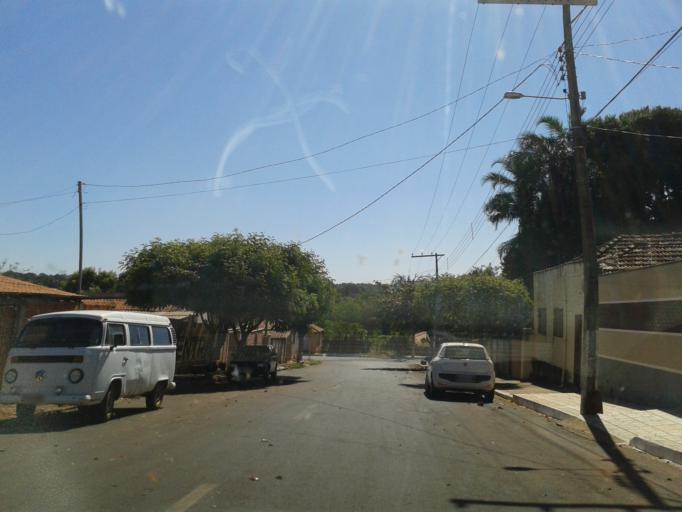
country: BR
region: Minas Gerais
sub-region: Santa Vitoria
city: Santa Vitoria
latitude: -18.8384
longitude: -50.1257
